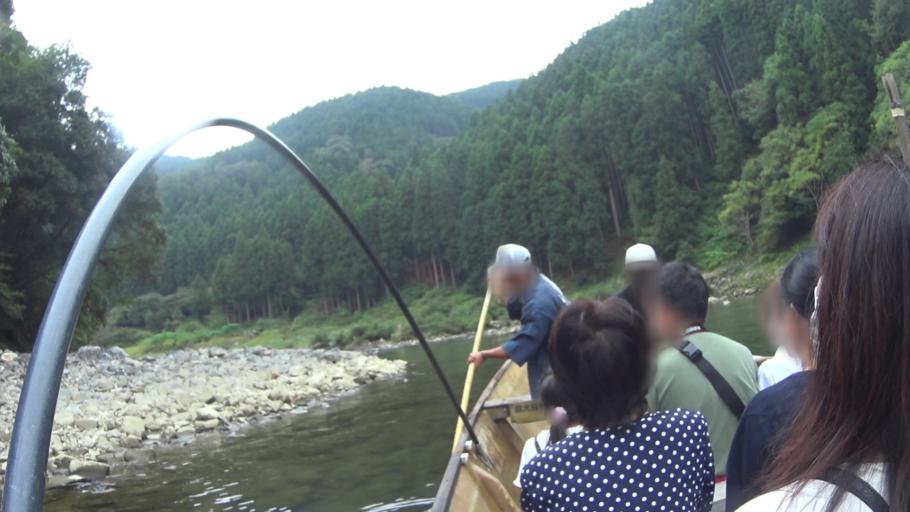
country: JP
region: Kyoto
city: Kameoka
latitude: 35.0188
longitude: 135.6315
